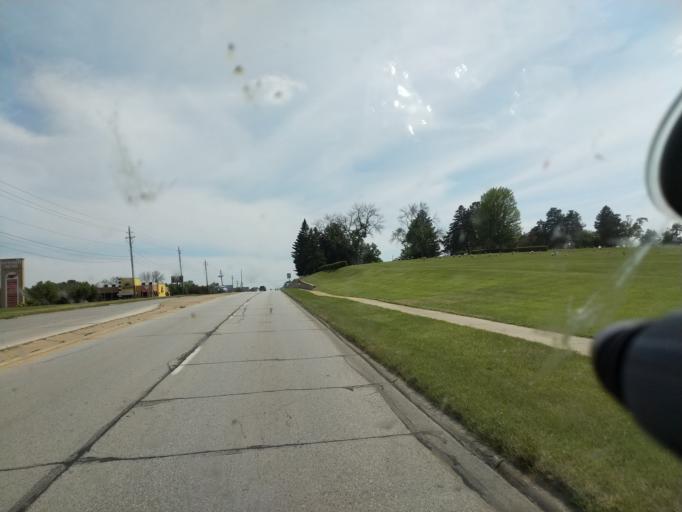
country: US
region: Iowa
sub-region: Polk County
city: Urbandale
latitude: 41.6400
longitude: -93.6977
